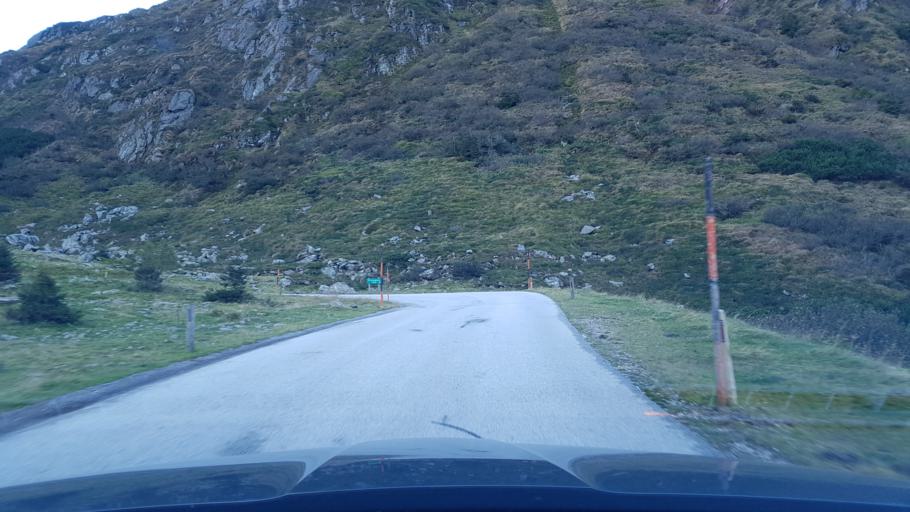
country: AT
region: Styria
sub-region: Politischer Bezirk Liezen
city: Sankt Nikolai im Solktal
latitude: 47.2749
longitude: 14.0808
